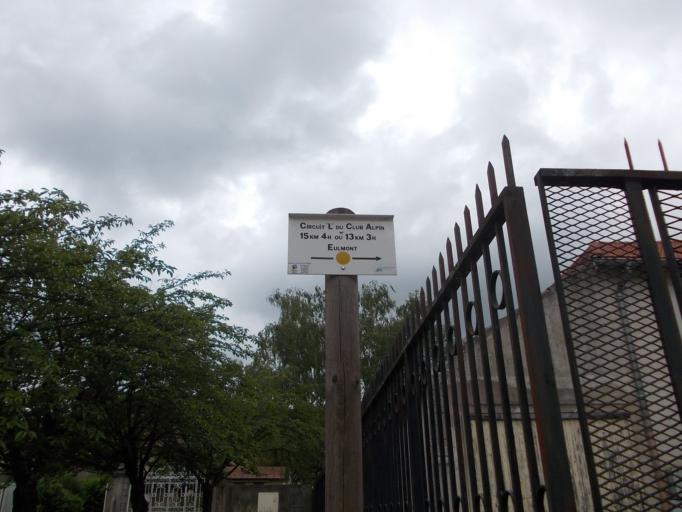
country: FR
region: Lorraine
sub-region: Departement de Meurthe-et-Moselle
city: Lay-Saint-Christophe
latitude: 48.7487
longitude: 6.2002
